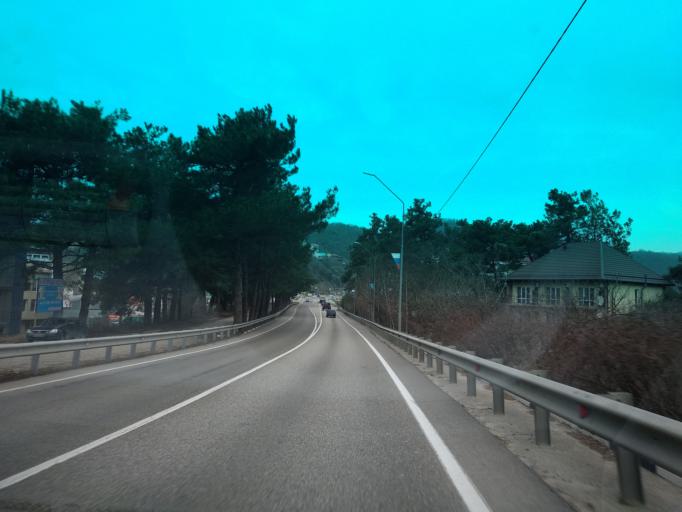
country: RU
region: Krasnodarskiy
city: Ol'ginka
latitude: 44.1973
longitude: 38.8911
